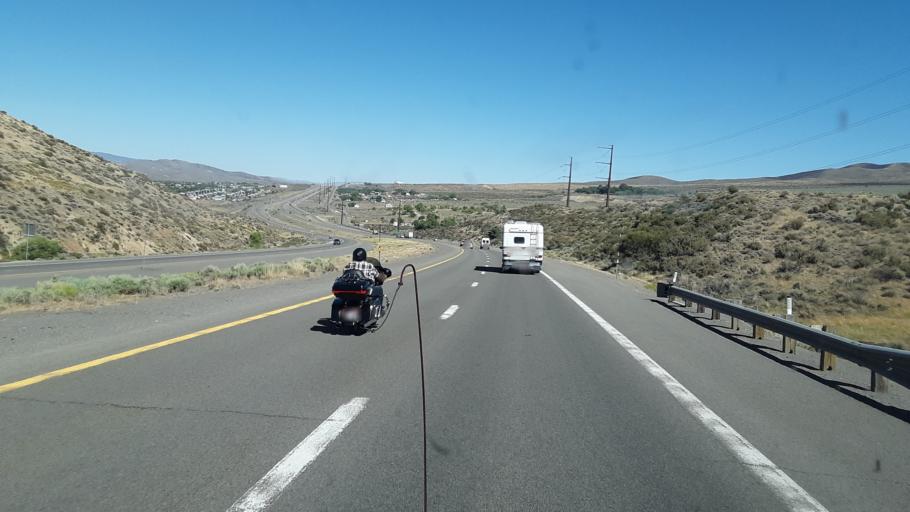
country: US
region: Nevada
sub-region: Washoe County
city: Cold Springs
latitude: 39.6280
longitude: -119.9296
